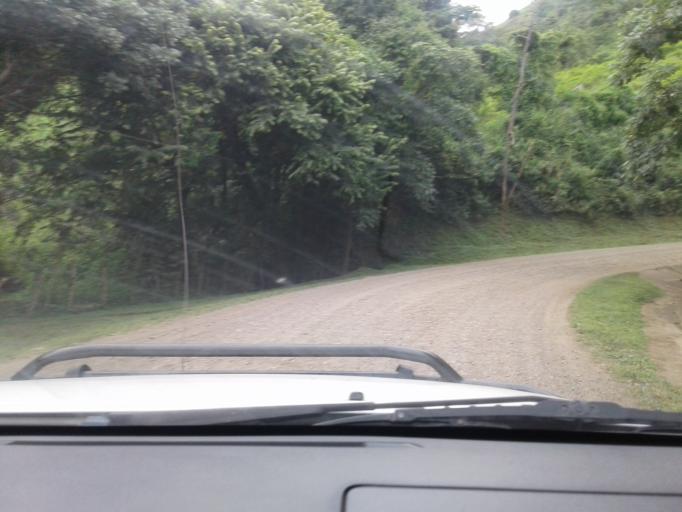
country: NI
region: Matagalpa
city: San Ramon
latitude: 12.9112
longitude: -85.8092
